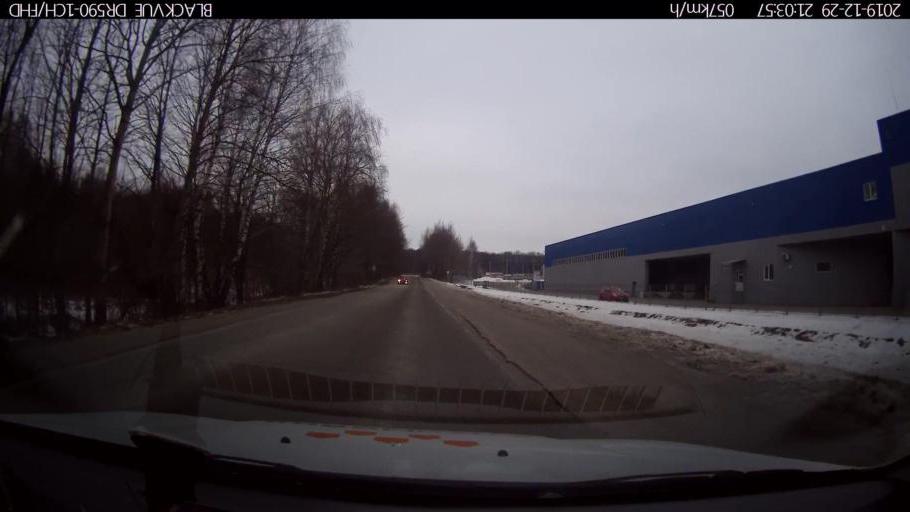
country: RU
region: Nizjnij Novgorod
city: Afonino
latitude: 56.1994
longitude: 44.0046
